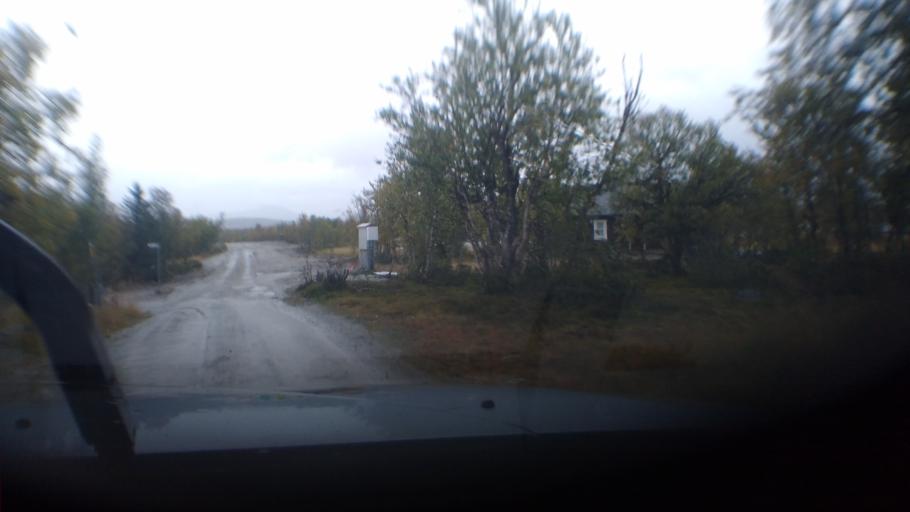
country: NO
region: Oppland
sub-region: Ringebu
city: Ringebu
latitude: 61.6535
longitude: 10.1017
